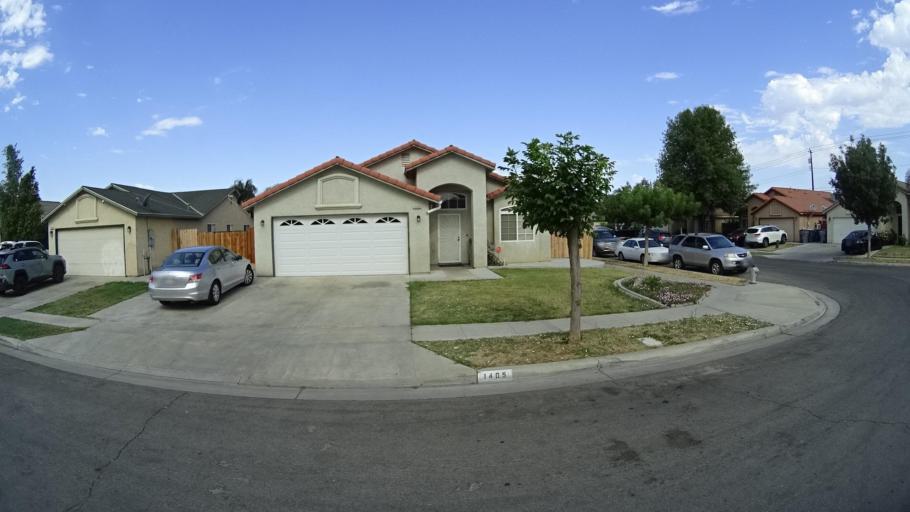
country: US
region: California
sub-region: Fresno County
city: Sunnyside
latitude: 36.7605
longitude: -119.7142
